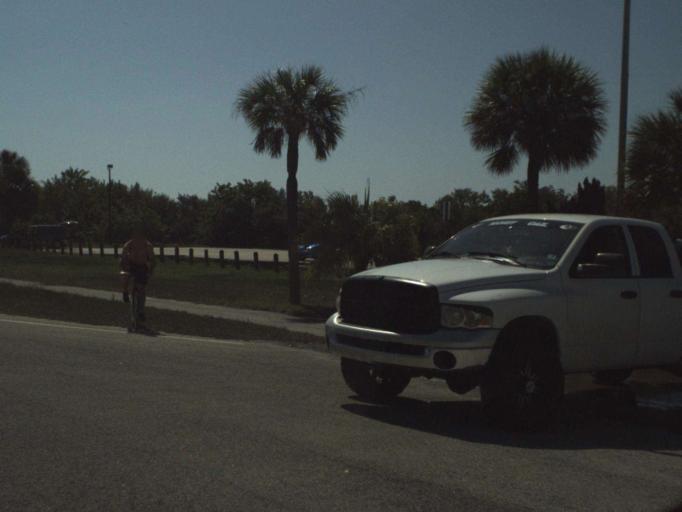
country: US
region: Florida
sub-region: Brevard County
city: Cocoa Beach
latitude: 28.3577
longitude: -80.6286
